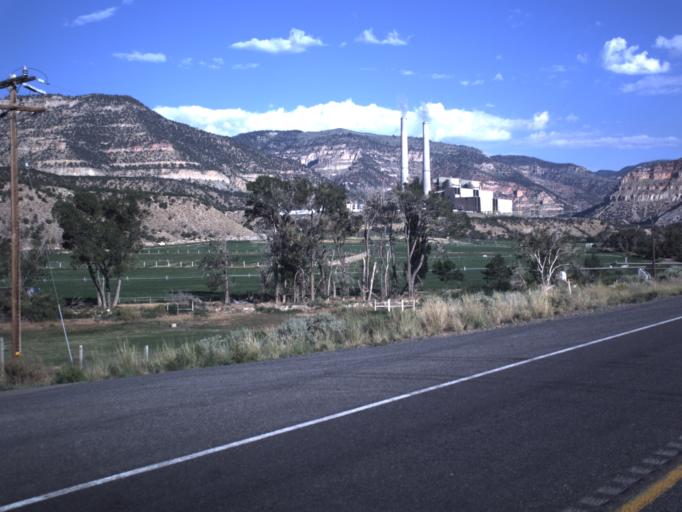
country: US
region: Utah
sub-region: Emery County
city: Huntington
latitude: 39.3723
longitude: -111.0619
